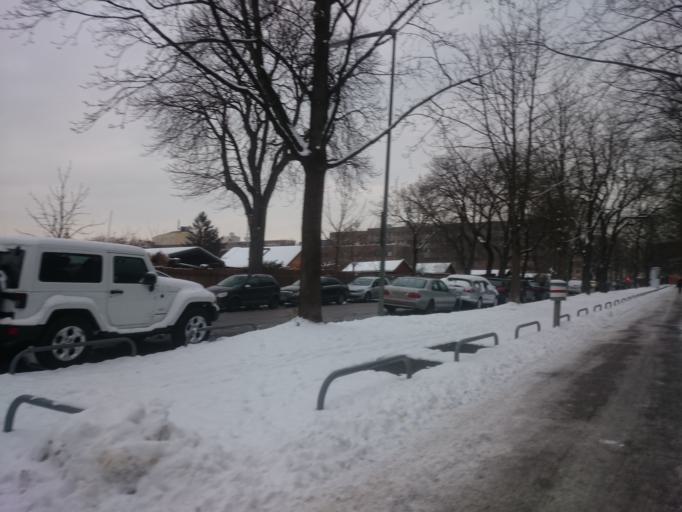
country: DE
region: Bavaria
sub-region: Upper Bavaria
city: Munich
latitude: 48.1533
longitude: 11.5491
